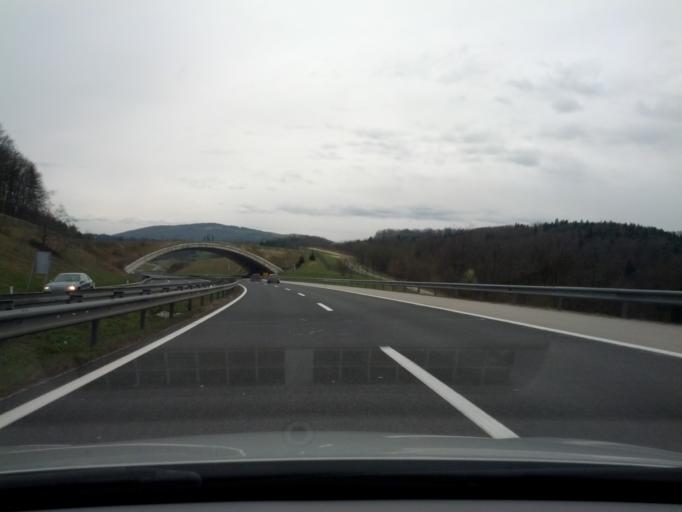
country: SI
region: Zuzemberk
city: Zuzemberk
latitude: 45.9256
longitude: 14.9319
